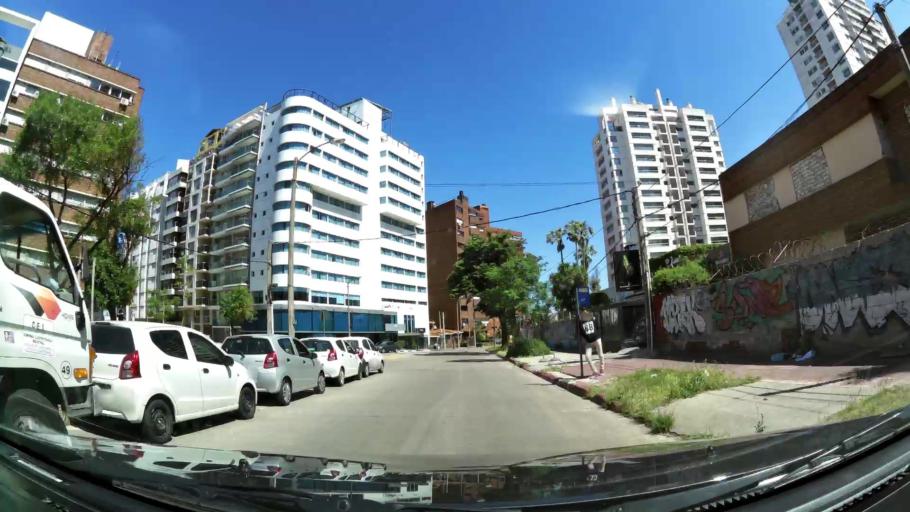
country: UY
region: Montevideo
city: Montevideo
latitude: -34.9037
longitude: -56.1331
